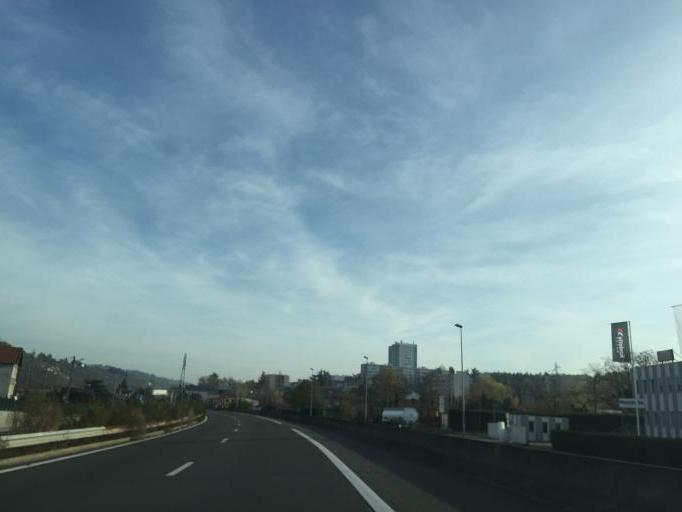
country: FR
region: Rhone-Alpes
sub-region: Departement de la Loire
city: Lorette
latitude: 45.5175
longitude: 4.5891
